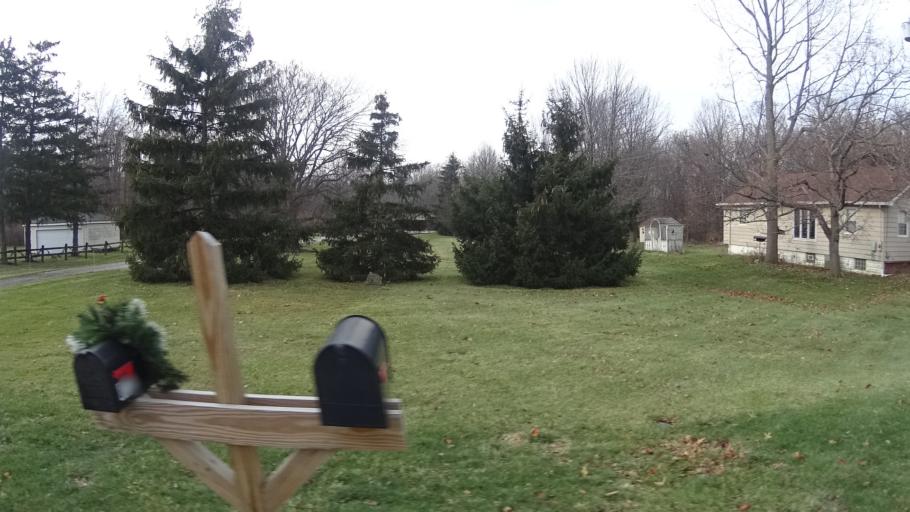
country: US
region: Ohio
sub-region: Lorain County
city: Amherst
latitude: 41.4023
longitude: -82.2018
